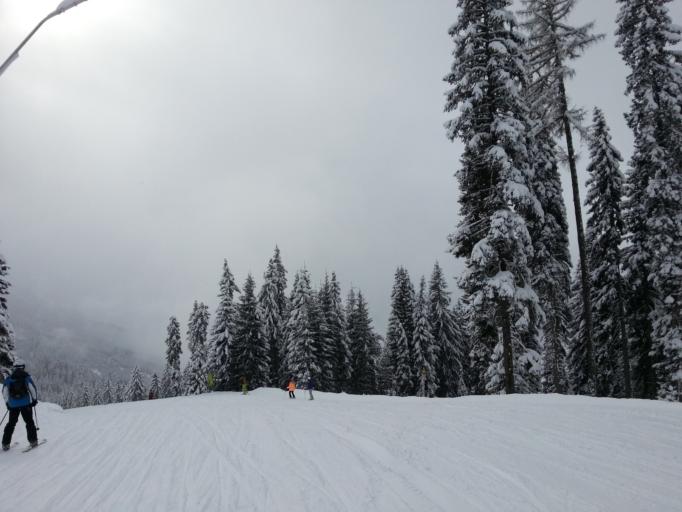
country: AT
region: Salzburg
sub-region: Politischer Bezirk Sankt Johann im Pongau
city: Kleinarl
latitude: 47.2940
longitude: 13.3307
